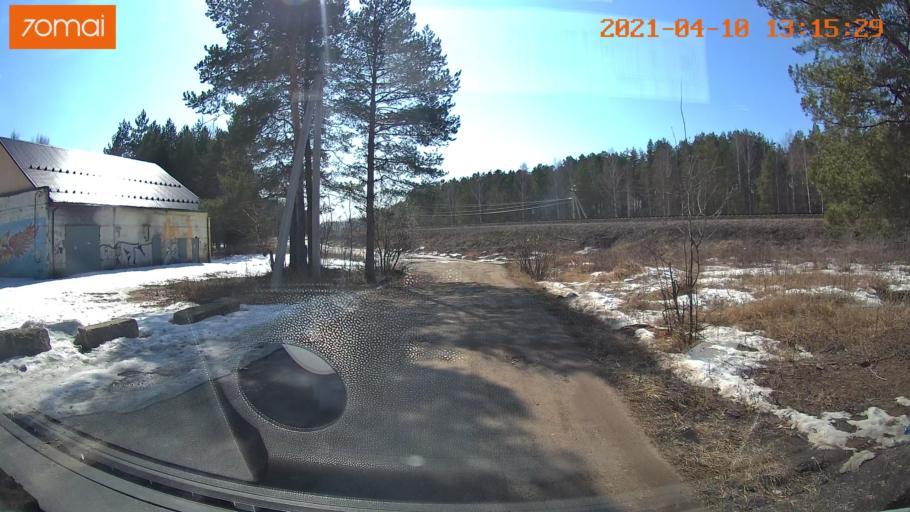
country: RU
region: Ivanovo
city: Bogorodskoye
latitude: 56.9972
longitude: 41.0605
